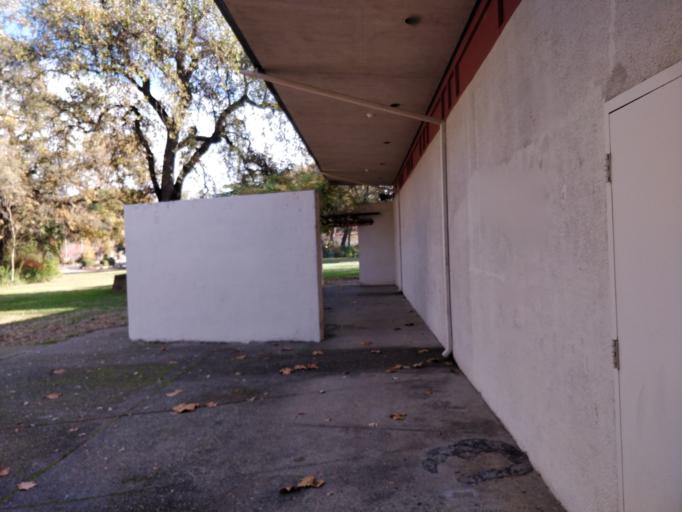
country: US
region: California
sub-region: Shasta County
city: Redding
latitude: 40.5945
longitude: -122.3967
